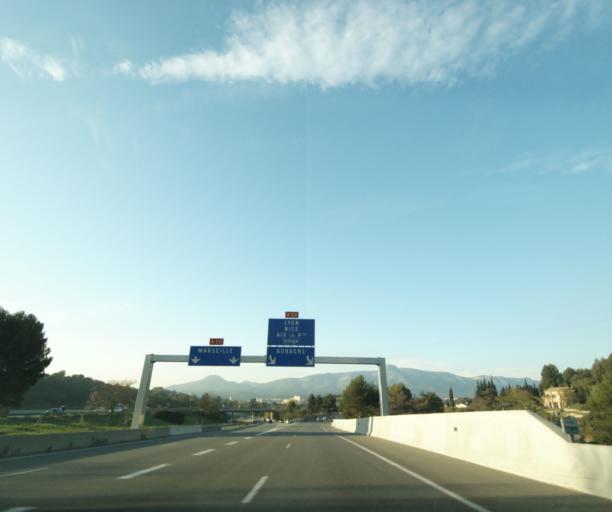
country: FR
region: Provence-Alpes-Cote d'Azur
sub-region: Departement des Bouches-du-Rhone
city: Aubagne
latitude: 43.2782
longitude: 5.5864
